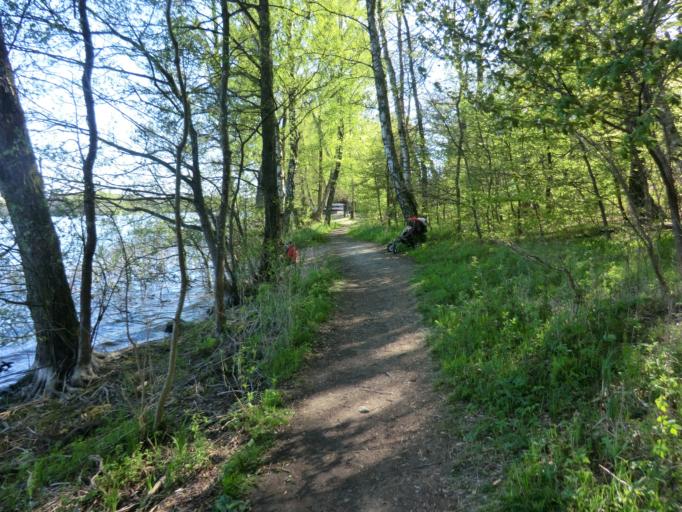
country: SE
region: Skane
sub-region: Sjobo Kommun
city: Sjoebo
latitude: 55.5668
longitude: 13.7180
